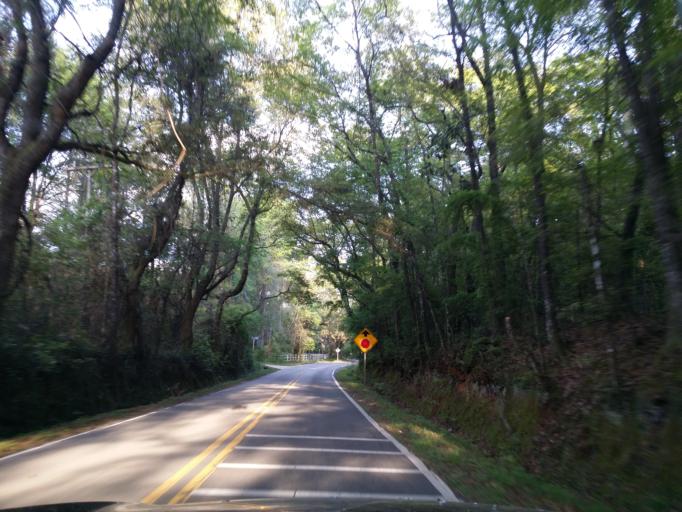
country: US
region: Florida
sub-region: Leon County
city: Tallahassee
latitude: 30.5221
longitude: -84.1107
